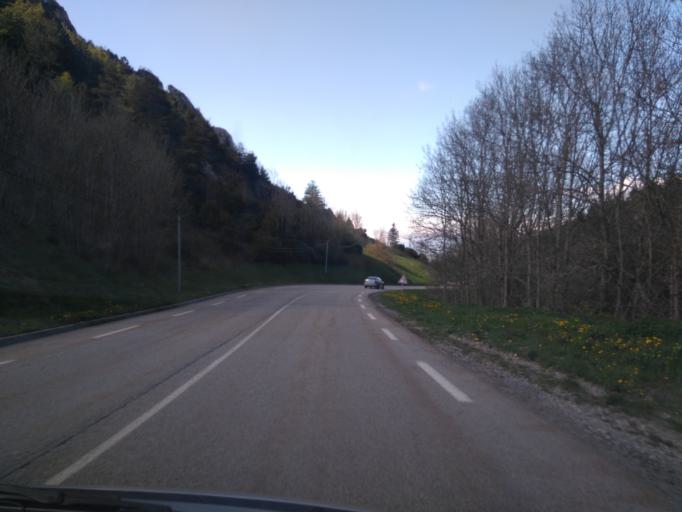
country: FR
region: Rhone-Alpes
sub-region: Departement de l'Isere
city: Mens
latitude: 44.7300
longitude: 5.6795
